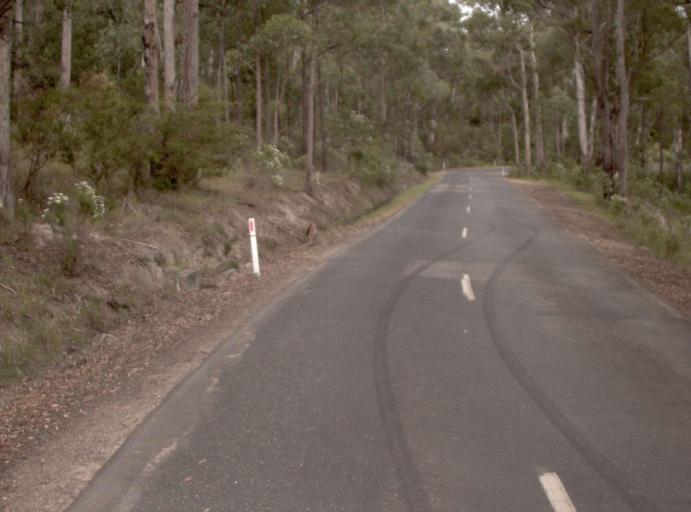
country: AU
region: Victoria
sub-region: East Gippsland
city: Bairnsdale
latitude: -37.7058
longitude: 147.5915
